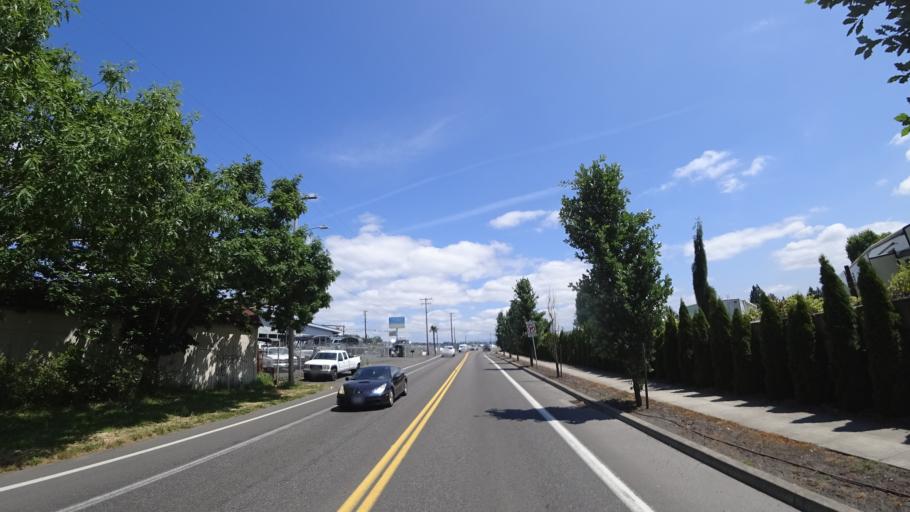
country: US
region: Washington
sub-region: Clark County
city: Vancouver
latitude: 45.6002
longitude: -122.6569
